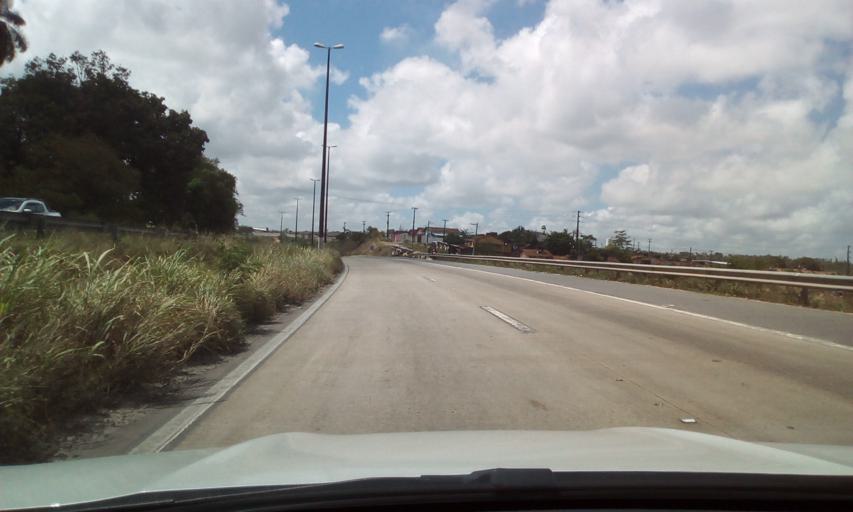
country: BR
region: Pernambuco
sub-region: Igarassu
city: Igarassu
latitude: -7.8122
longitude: -34.9190
